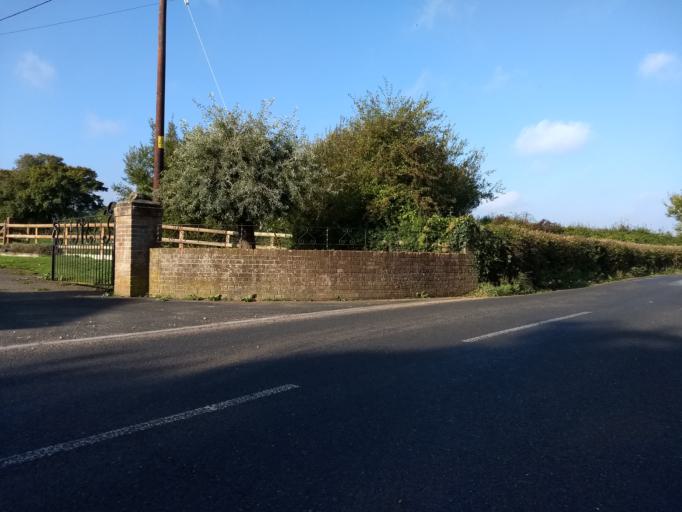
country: GB
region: England
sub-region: Isle of Wight
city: Ryde
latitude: 50.7186
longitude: -1.1921
